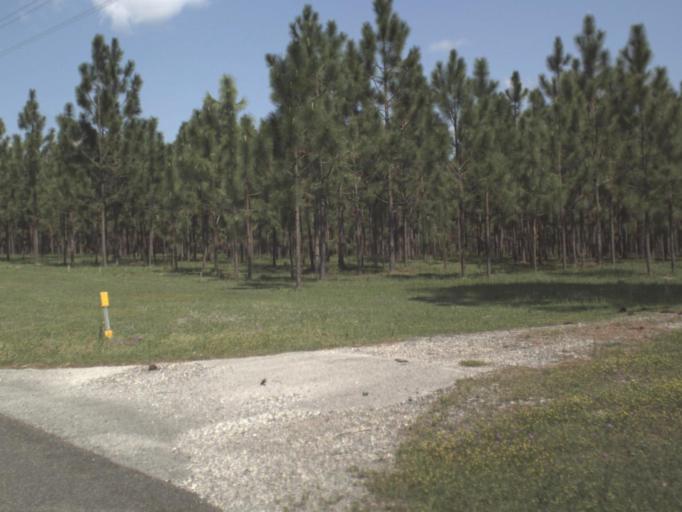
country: US
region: Florida
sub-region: Santa Rosa County
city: Point Baker
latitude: 30.8911
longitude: -86.9781
